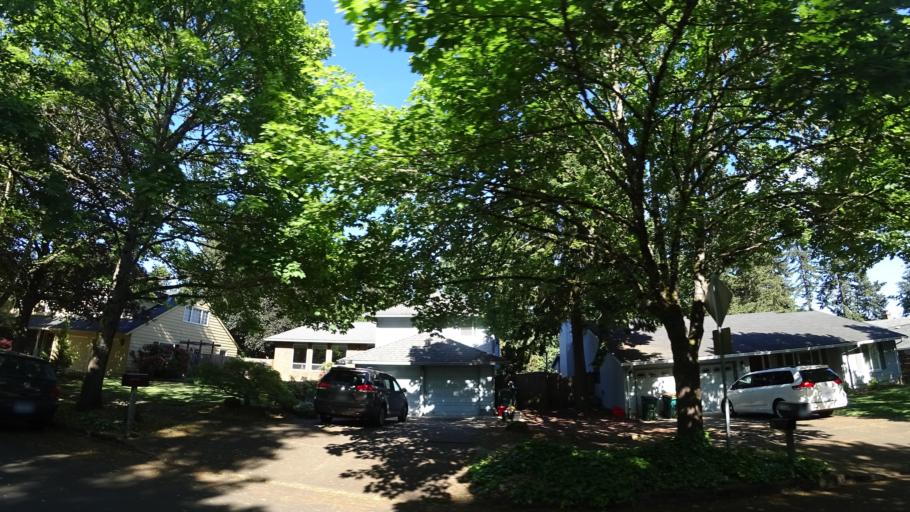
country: US
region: Oregon
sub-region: Washington County
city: Beaverton
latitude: 45.4497
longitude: -122.8175
